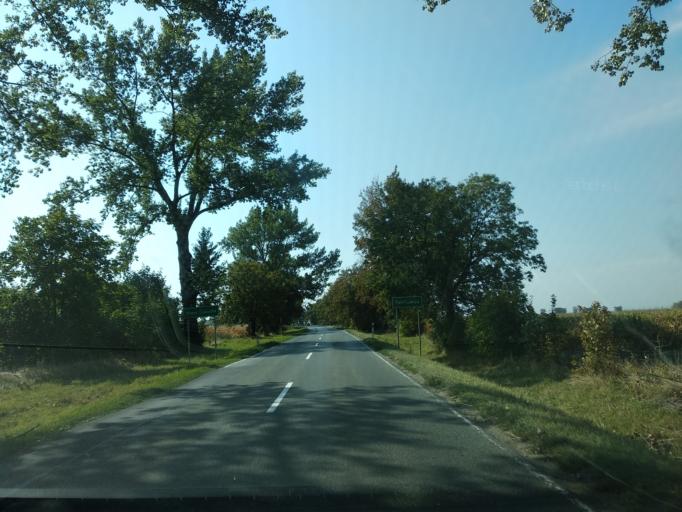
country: PL
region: Lower Silesian Voivodeship
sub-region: Powiat wroclawski
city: Zorawina
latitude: 50.9390
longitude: 17.0698
